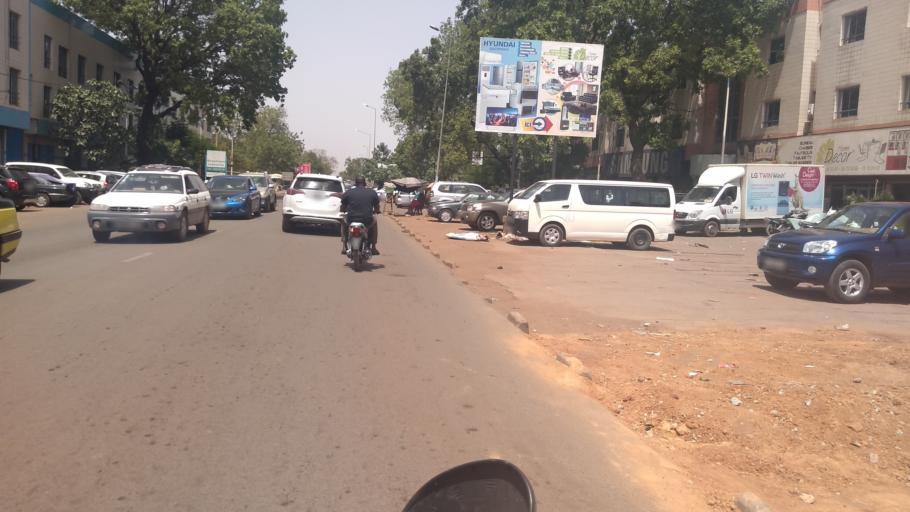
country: ML
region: Bamako
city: Bamako
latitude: 12.6424
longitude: -8.0202
